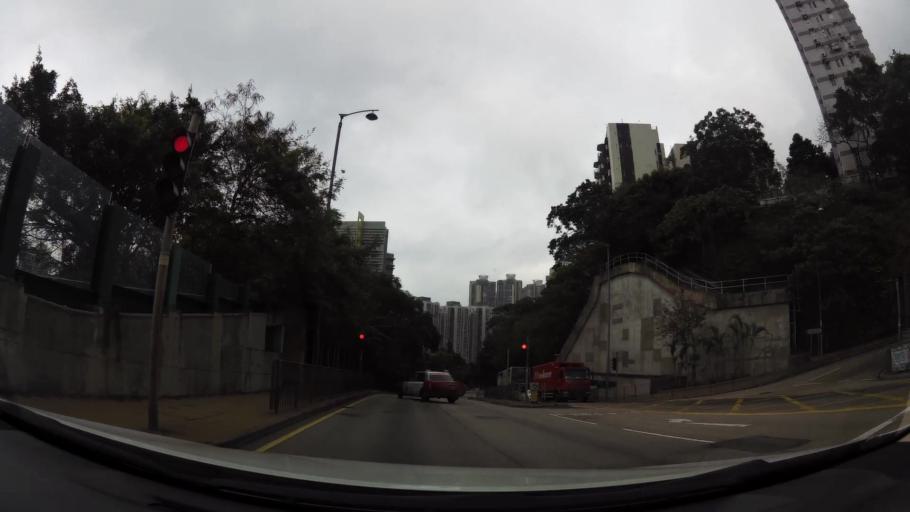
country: HK
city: Hong Kong
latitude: 22.2788
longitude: 114.1311
